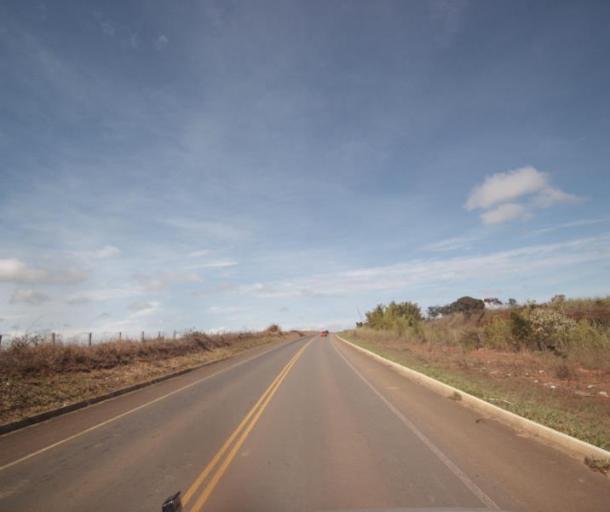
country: BR
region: Goias
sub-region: Anapolis
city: Anapolis
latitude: -16.1810
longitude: -48.9021
